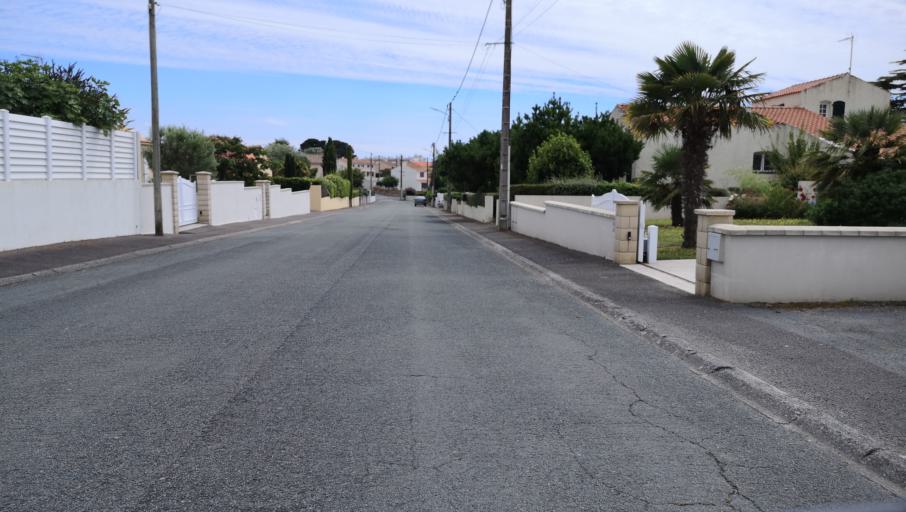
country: FR
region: Pays de la Loire
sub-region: Departement de la Vendee
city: Les Sables-d'Olonne
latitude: 46.5052
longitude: -1.7687
